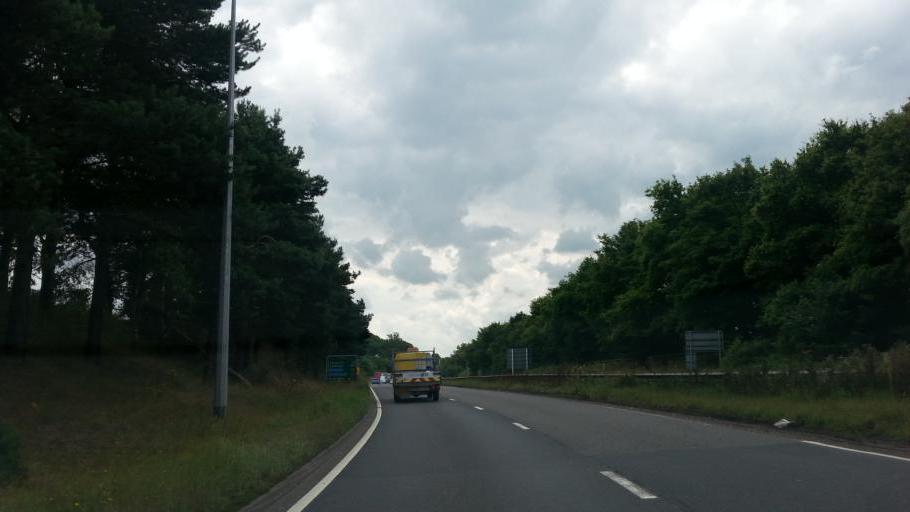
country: GB
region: England
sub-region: Staffordshire
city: Lichfield
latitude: 52.6619
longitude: -1.8139
